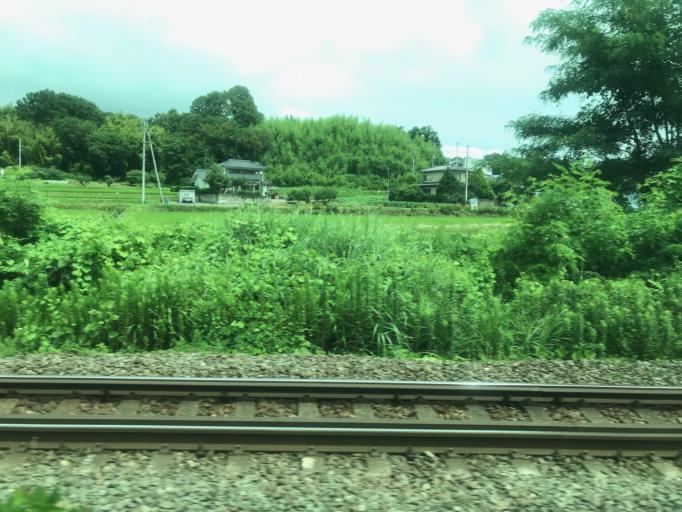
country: JP
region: Fukushima
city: Koriyama
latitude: 37.4495
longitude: 140.3862
